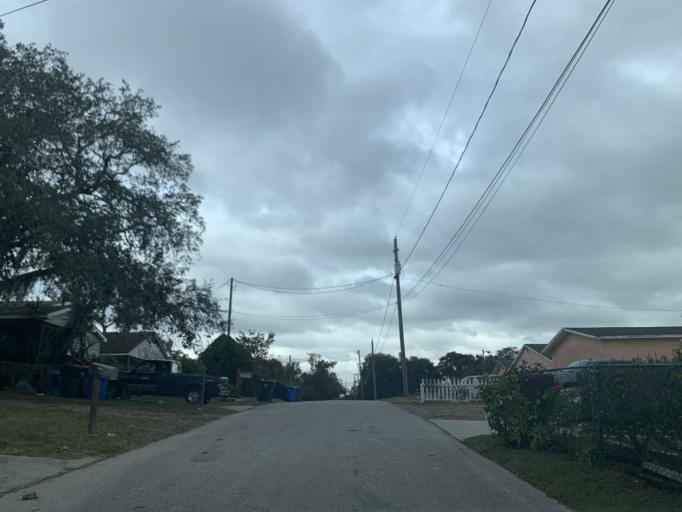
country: US
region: Florida
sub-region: Hillsborough County
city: East Lake-Orient Park
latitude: 27.9786
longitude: -82.3928
